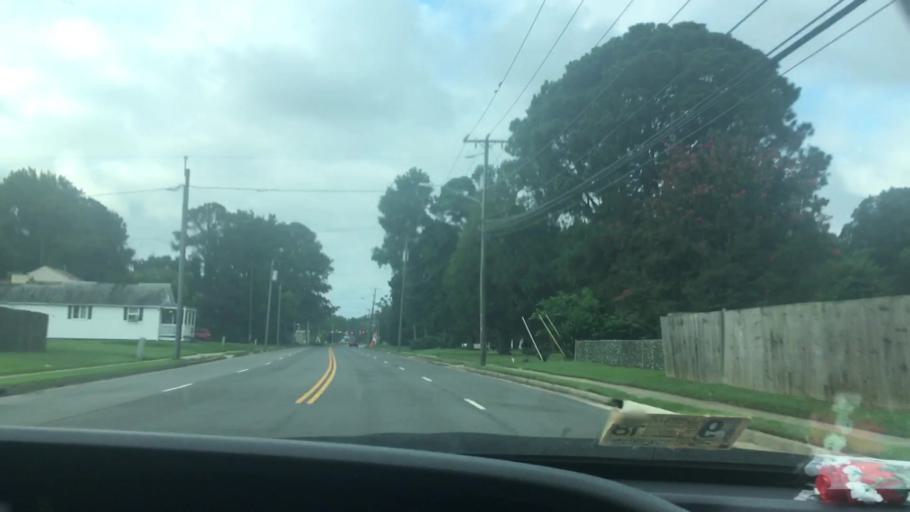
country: US
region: Virginia
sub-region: City of Hampton
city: East Hampton
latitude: 37.0361
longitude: -76.3221
